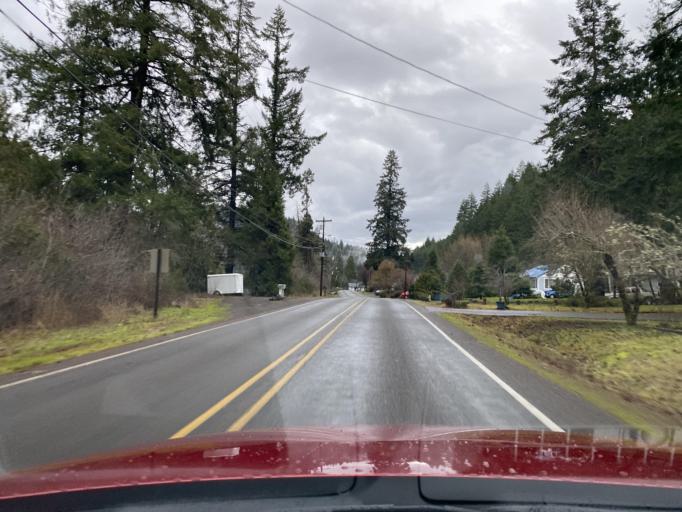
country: US
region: Oregon
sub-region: Lane County
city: Oakridge
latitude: 43.7563
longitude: -122.5067
